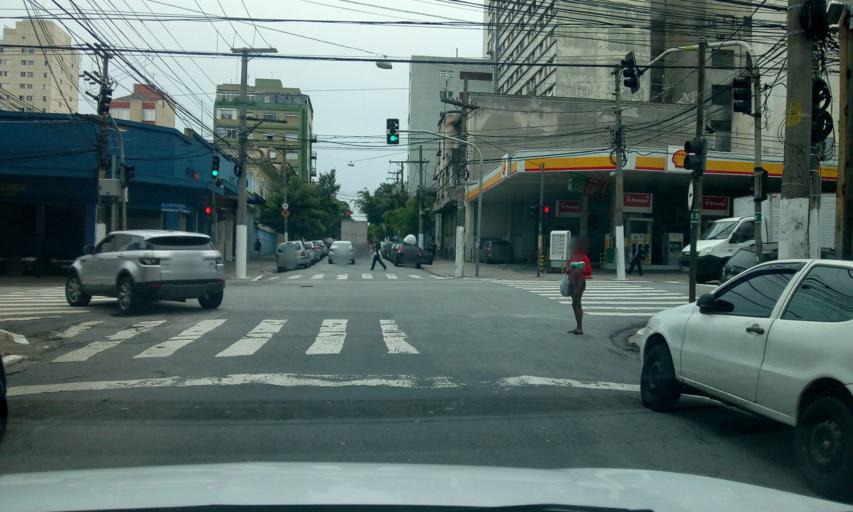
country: BR
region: Sao Paulo
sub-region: Sao Paulo
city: Sao Paulo
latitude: -23.5354
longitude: -46.6473
